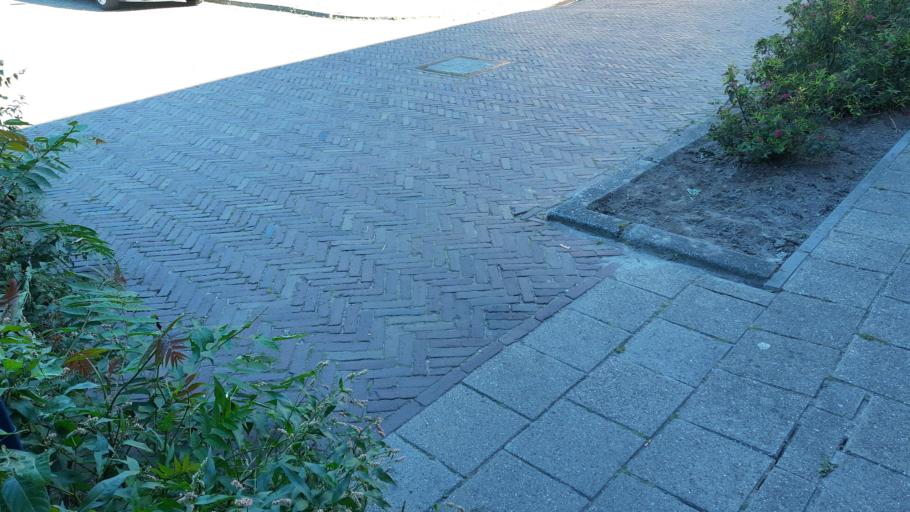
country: NL
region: North Holland
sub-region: Gemeente Enkhuizen
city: Enkhuizen
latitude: 52.7033
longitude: 5.2831
